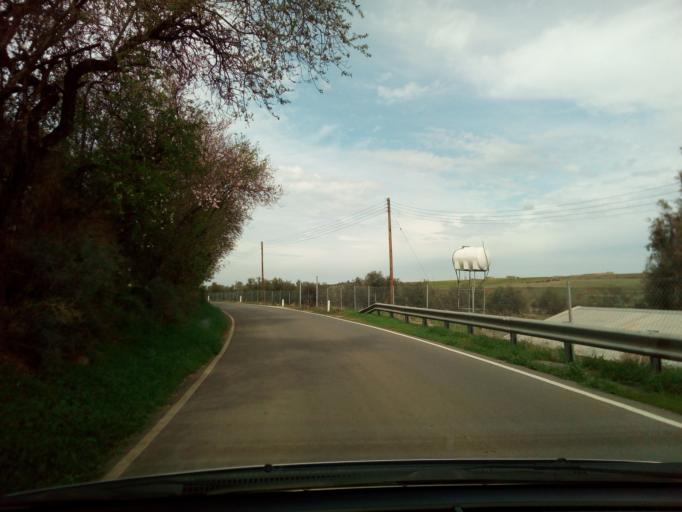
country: CY
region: Lefkosia
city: Astromeritis
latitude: 35.0974
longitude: 32.9854
